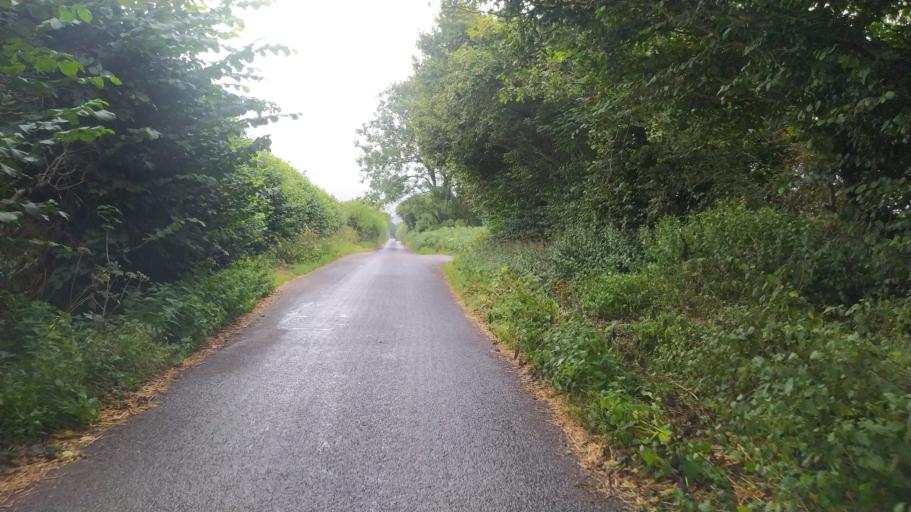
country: GB
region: England
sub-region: Wiltshire
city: Ansty
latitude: 51.0131
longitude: -2.1154
